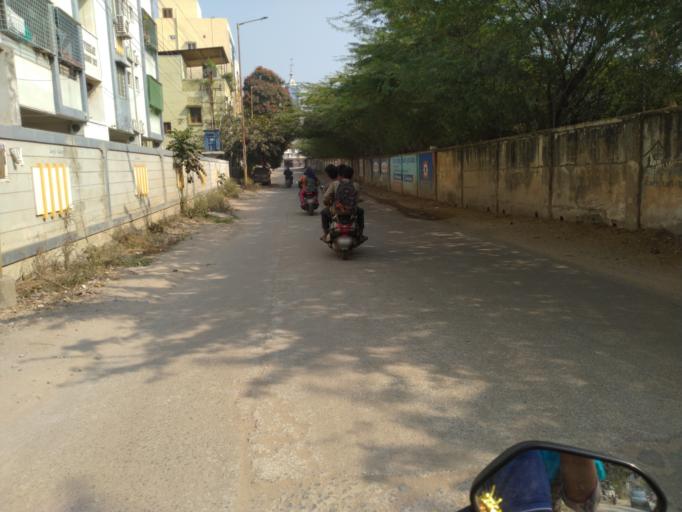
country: IN
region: Telangana
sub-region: Rangareddi
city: Quthbullapur
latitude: 17.4983
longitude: 78.4691
